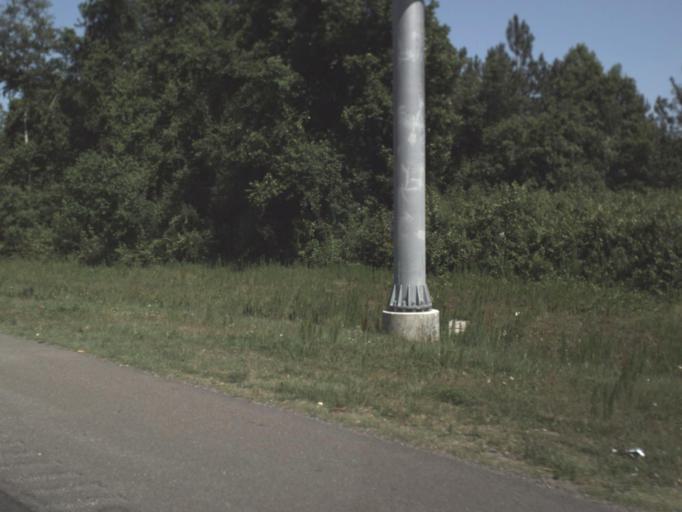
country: US
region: Florida
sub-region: Clay County
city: Bellair-Meadowbrook Terrace
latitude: 30.3129
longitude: -81.8133
